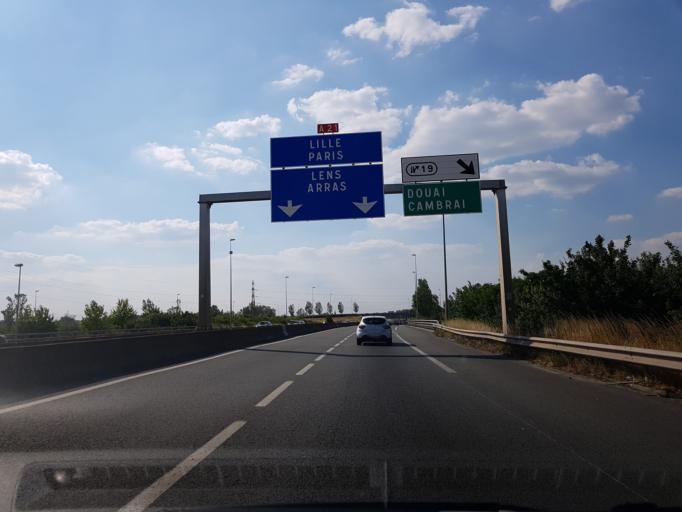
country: FR
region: Nord-Pas-de-Calais
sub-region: Departement du Nord
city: Auby
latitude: 50.4066
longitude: 3.0411
